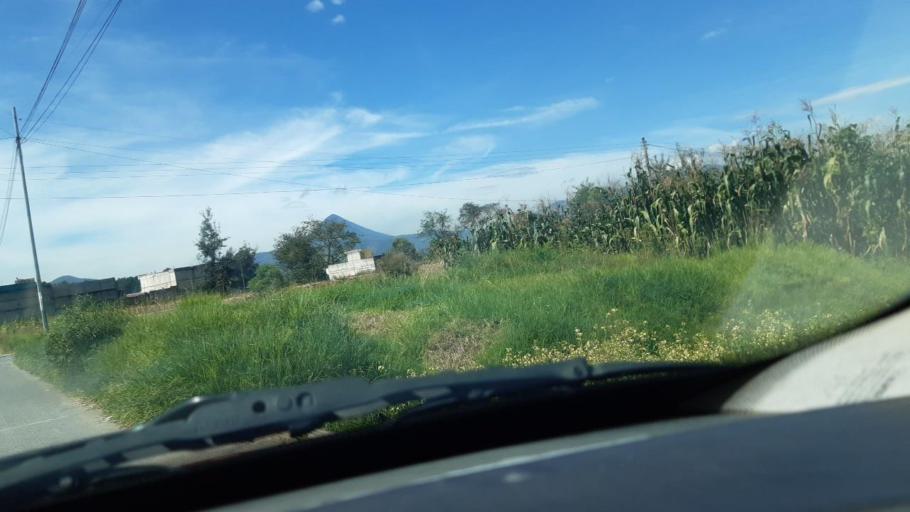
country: GT
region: Quetzaltenango
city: Salcaja
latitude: 14.8845
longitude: -91.4508
